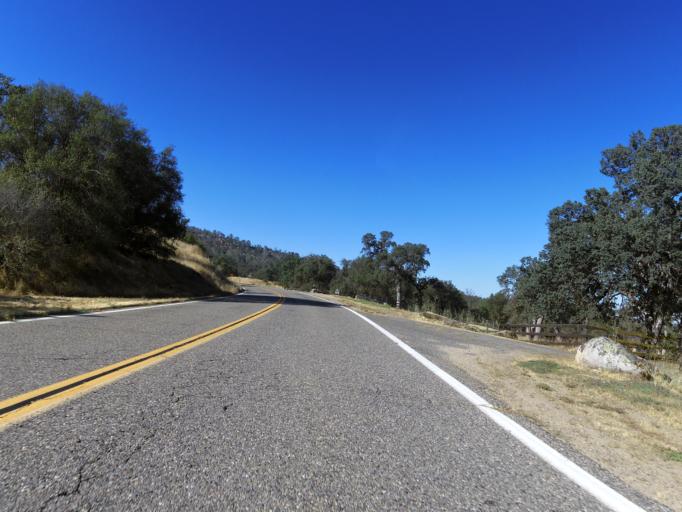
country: US
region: California
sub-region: Madera County
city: Yosemite Lakes
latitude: 37.2000
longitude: -119.8000
